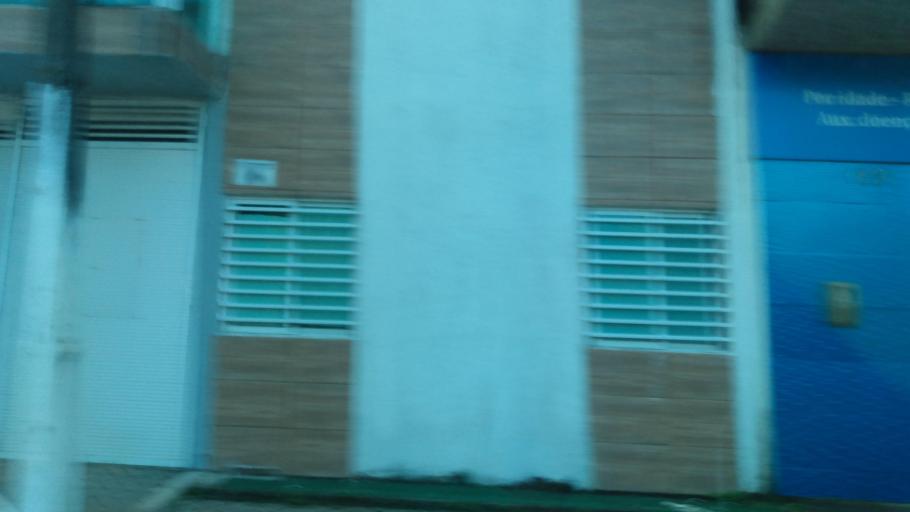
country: BR
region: Pernambuco
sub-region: Palmares
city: Palmares
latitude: -8.6876
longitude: -35.5979
